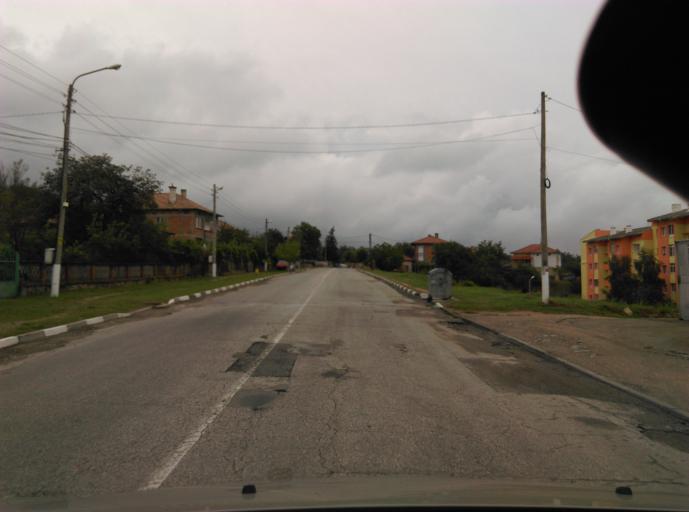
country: BG
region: Plovdiv
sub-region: Obshtina Karlovo
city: Karlovo
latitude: 42.6569
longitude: 24.7207
